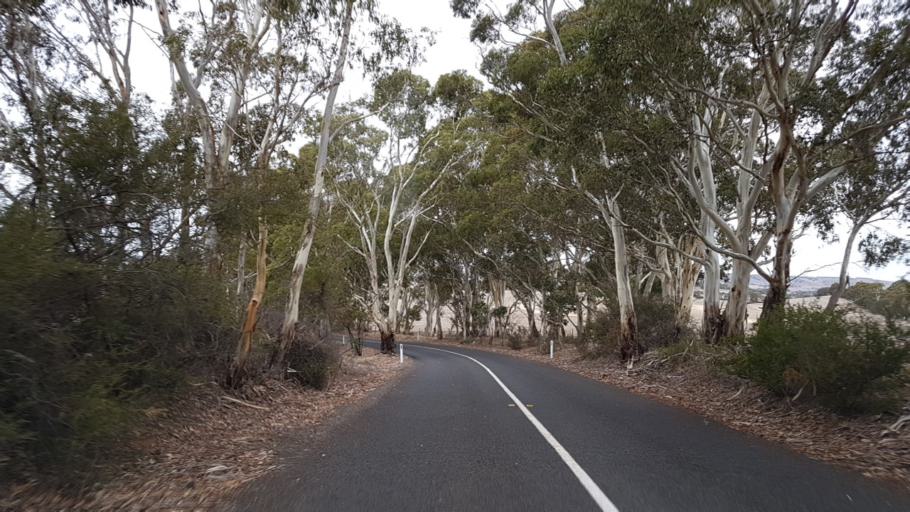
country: AU
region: South Australia
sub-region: Mount Barker
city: Nairne
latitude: -34.9855
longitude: 138.9902
